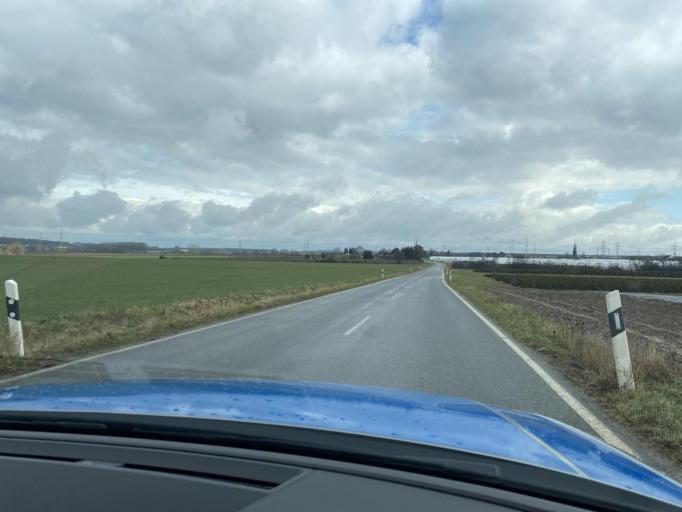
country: DE
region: North Rhine-Westphalia
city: Meckenheim
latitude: 50.5896
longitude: 7.0466
